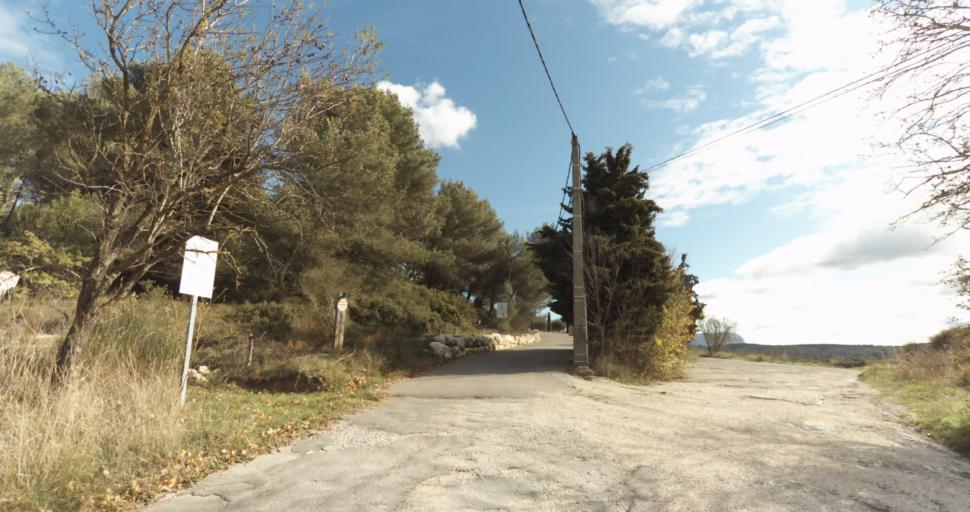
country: FR
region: Provence-Alpes-Cote d'Azur
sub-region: Departement des Bouches-du-Rhone
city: Venelles
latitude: 43.5896
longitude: 5.4877
